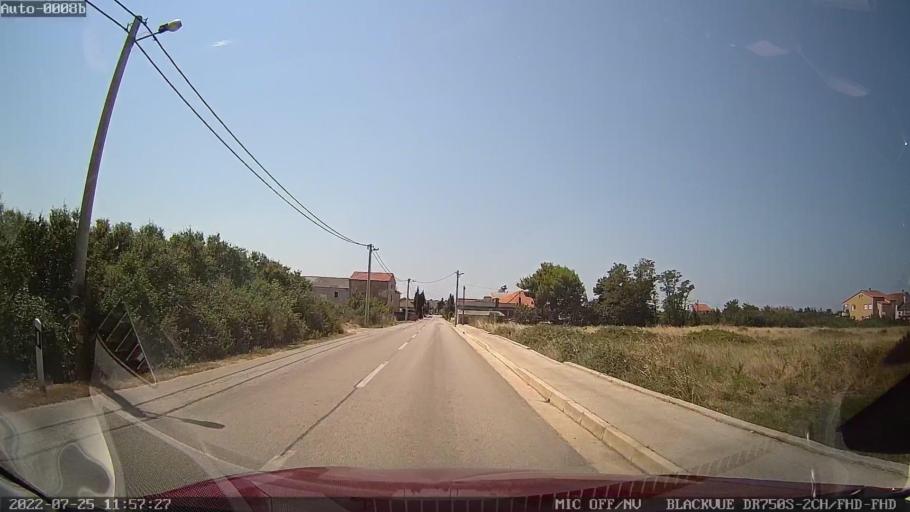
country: HR
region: Zadarska
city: Vrsi
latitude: 44.2432
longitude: 15.2142
